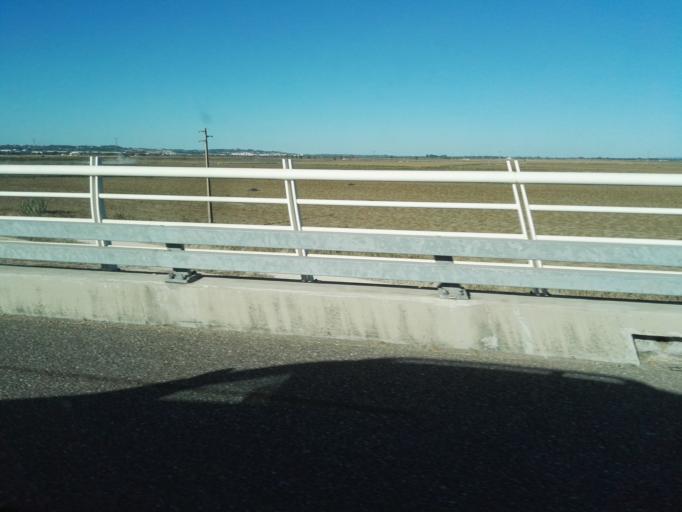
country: PT
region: Lisbon
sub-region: Vila Franca de Xira
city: Castanheira do Ribatejo
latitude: 39.0021
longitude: -8.9073
